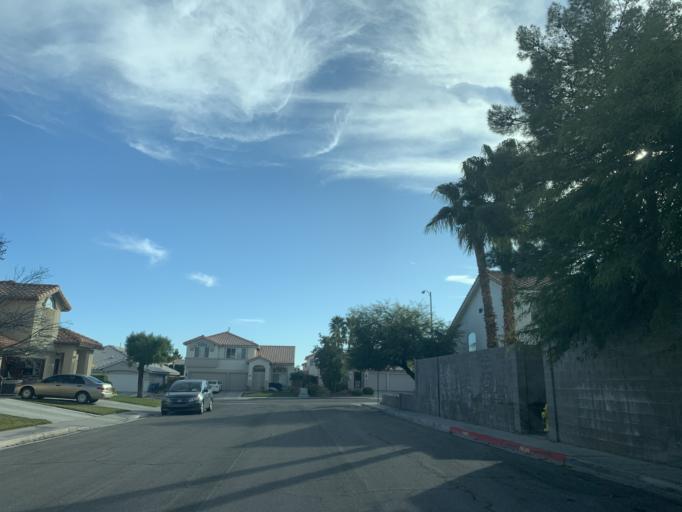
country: US
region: Nevada
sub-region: Clark County
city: Summerlin South
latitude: 36.1285
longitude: -115.3054
